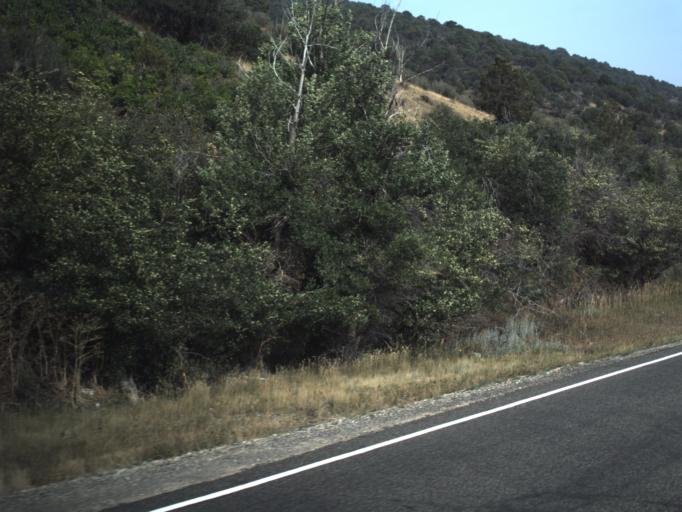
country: US
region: Utah
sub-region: Summit County
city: Francis
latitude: 40.6206
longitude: -111.2202
